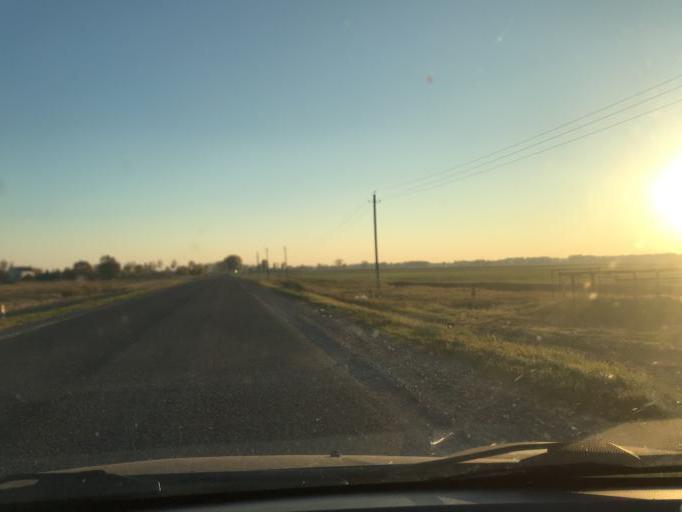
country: BY
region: Gomel
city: Brahin
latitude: 51.7827
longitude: 30.2533
